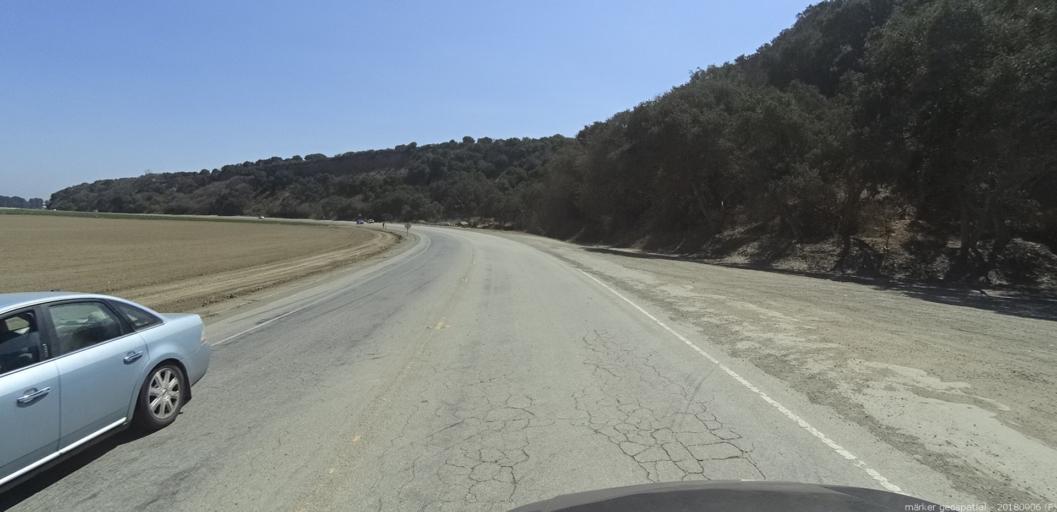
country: US
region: California
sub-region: Monterey County
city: Boronda
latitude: 36.6438
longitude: -121.7157
